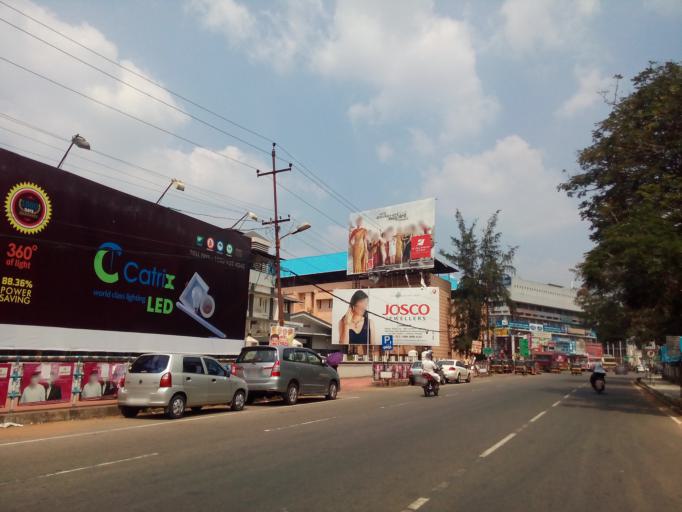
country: IN
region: Kerala
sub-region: Thrissur District
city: Trichur
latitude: 10.5271
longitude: 76.2135
